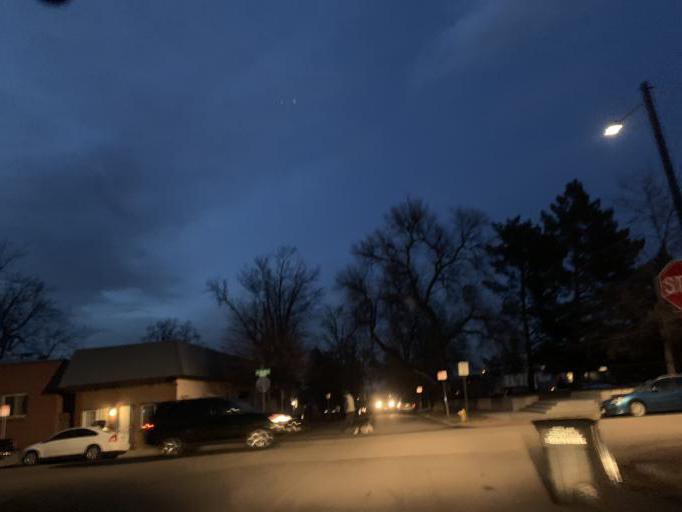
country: US
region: Colorado
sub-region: Jefferson County
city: Edgewater
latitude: 39.7728
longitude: -105.0451
